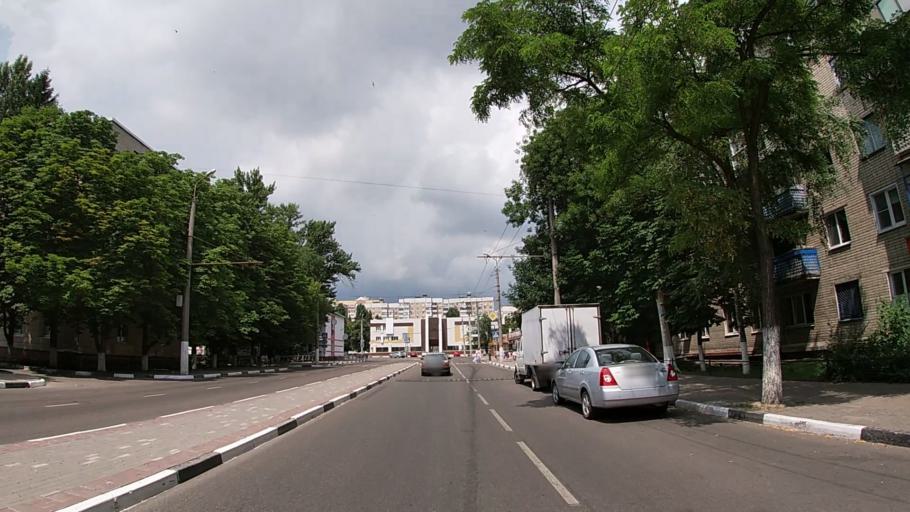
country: RU
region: Belgorod
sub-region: Belgorodskiy Rayon
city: Belgorod
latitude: 50.6122
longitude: 36.5911
